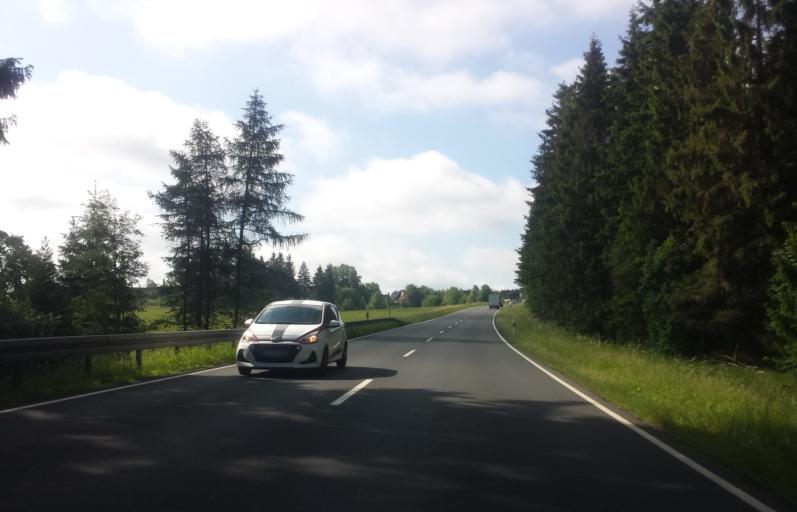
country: DE
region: Bavaria
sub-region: Upper Franconia
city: Ludwigsstadt
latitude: 50.4468
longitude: 11.3742
